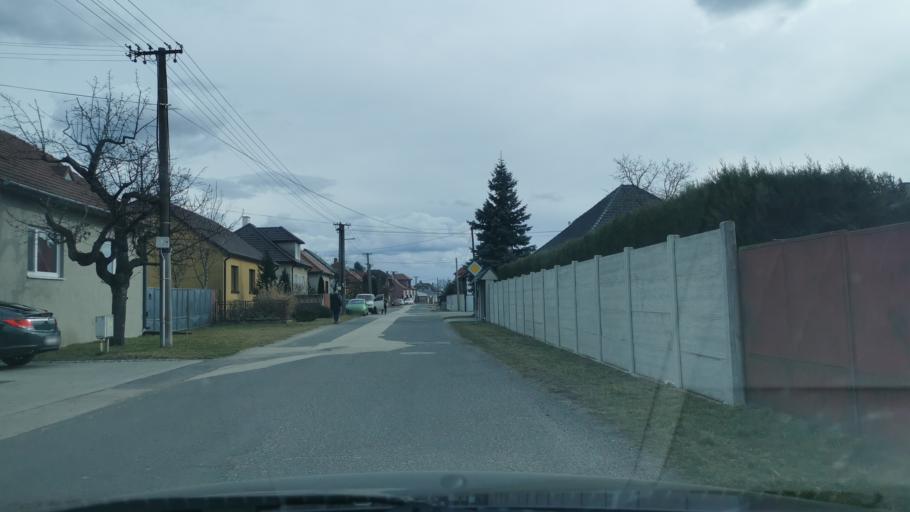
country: CZ
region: South Moravian
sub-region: Okres Breclav
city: Lanzhot
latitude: 48.6916
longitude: 17.0217
